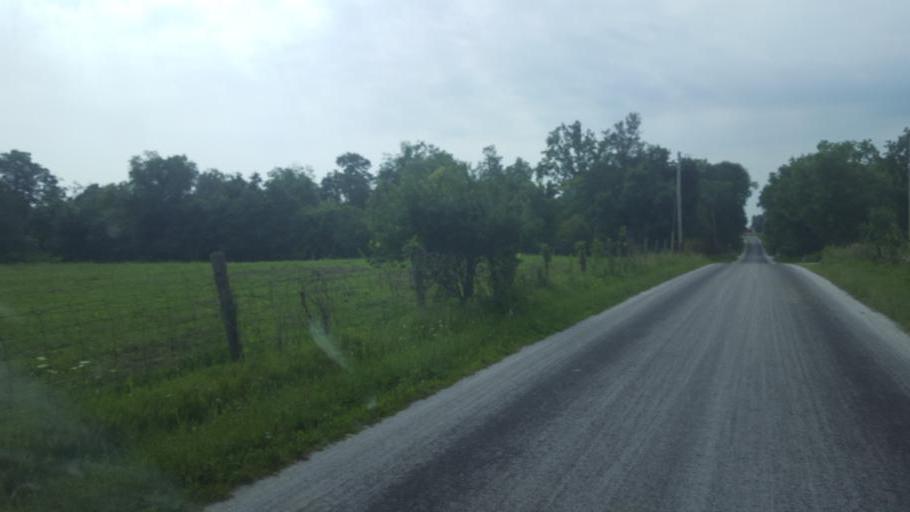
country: US
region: Ohio
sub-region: Hardin County
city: Kenton
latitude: 40.6162
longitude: -83.5284
